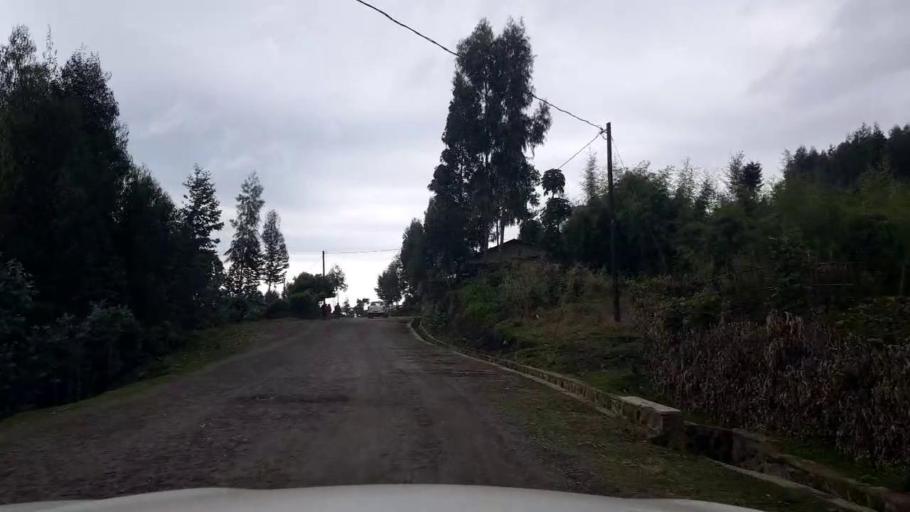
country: RW
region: Northern Province
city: Musanze
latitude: -1.4885
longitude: 29.5290
